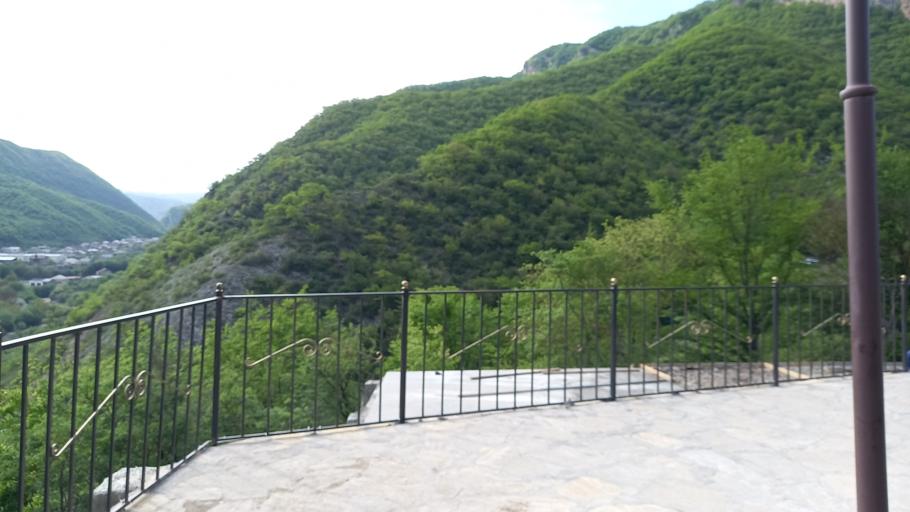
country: RU
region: Dagestan
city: Khuchni
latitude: 41.9646
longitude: 47.9563
